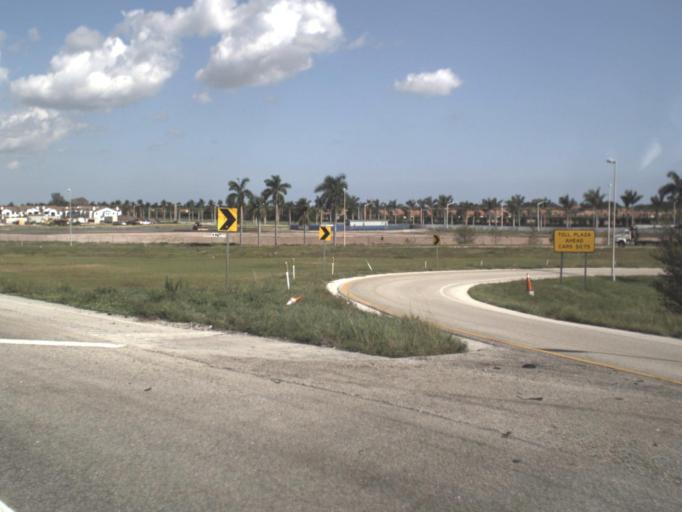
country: US
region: Florida
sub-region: Palm Beach County
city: Villages of Oriole
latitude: 26.4565
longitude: -80.1745
